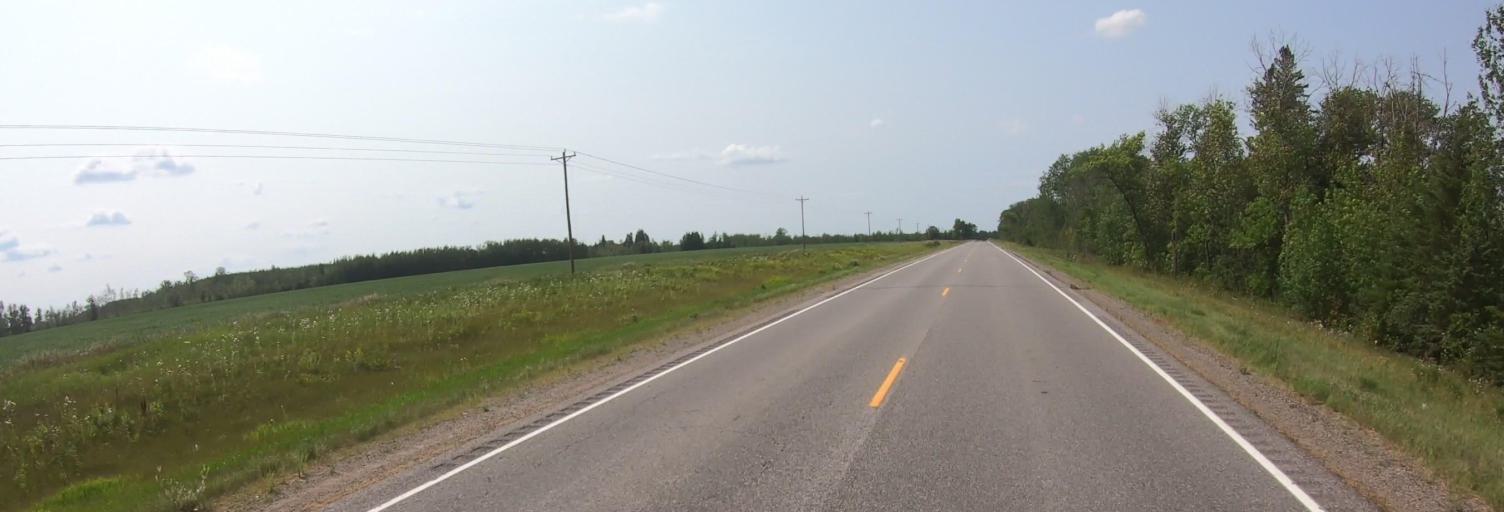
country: US
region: Minnesota
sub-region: Lake of the Woods County
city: Baudette
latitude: 48.6485
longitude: -94.2042
